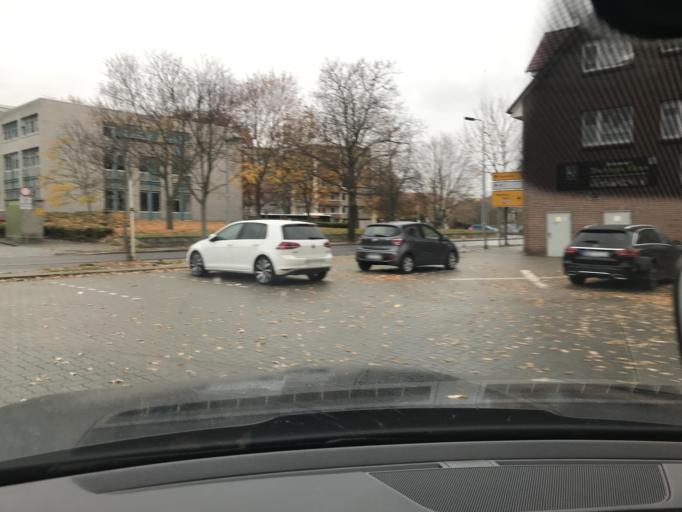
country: DE
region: Saxony-Anhalt
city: Halberstadt
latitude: 51.8959
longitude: 11.0607
